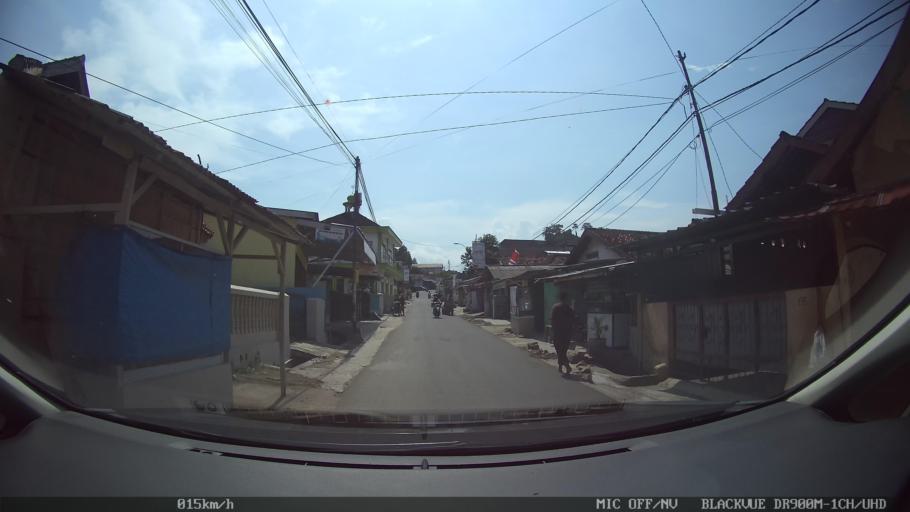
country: ID
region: Lampung
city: Kedaton
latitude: -5.3977
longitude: 105.2565
